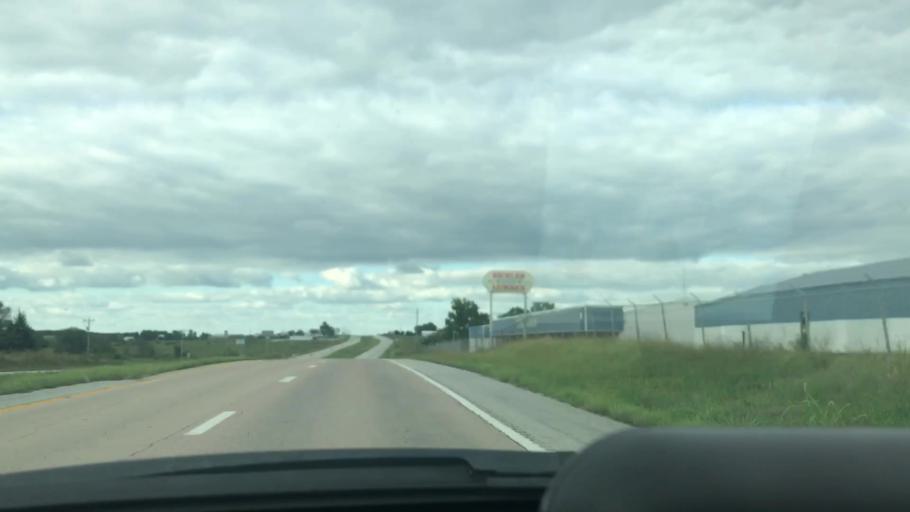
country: US
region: Missouri
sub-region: Benton County
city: Lincoln
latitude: 38.3314
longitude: -93.3414
